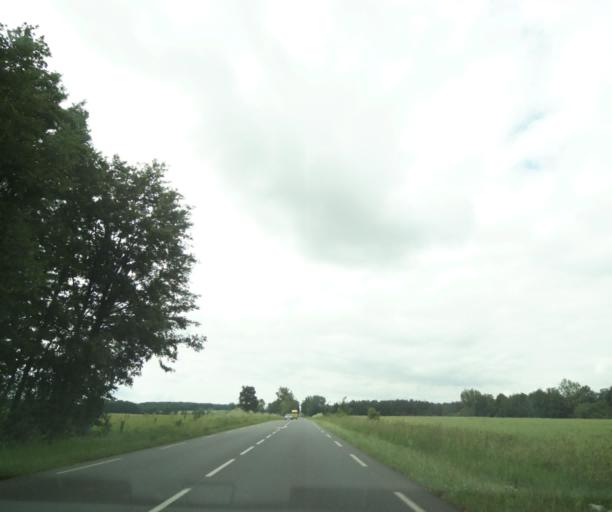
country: FR
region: Pays de la Loire
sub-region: Departement de Maine-et-Loire
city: Montreuil-Bellay
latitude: 47.1710
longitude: -0.1385
